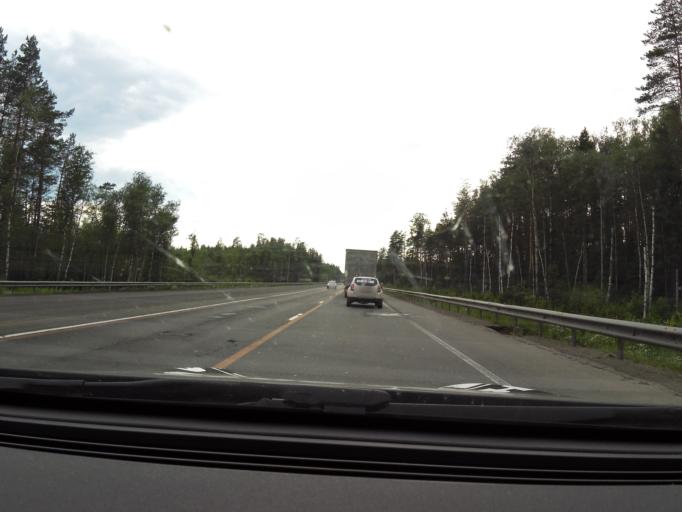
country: RU
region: Vladimir
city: Nikologory
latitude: 56.2351
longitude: 41.8761
